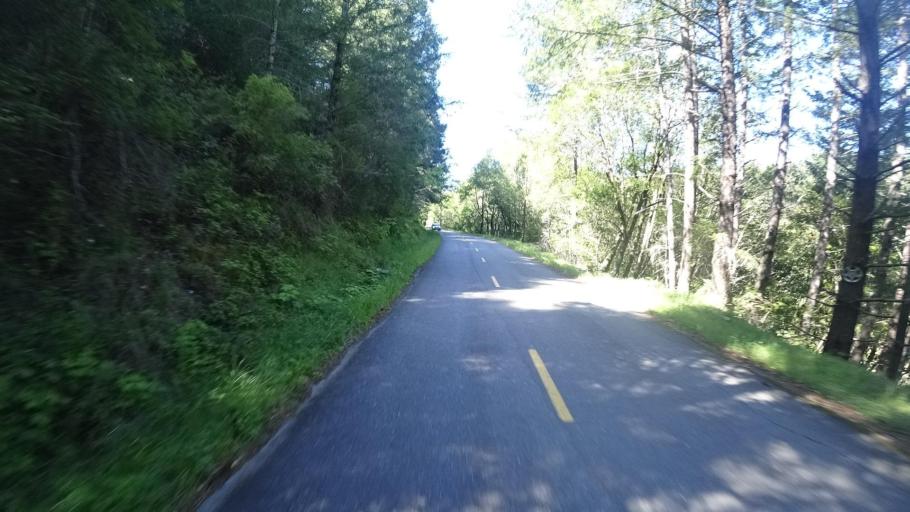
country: US
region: California
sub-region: Humboldt County
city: Rio Dell
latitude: 40.2370
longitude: -124.1348
